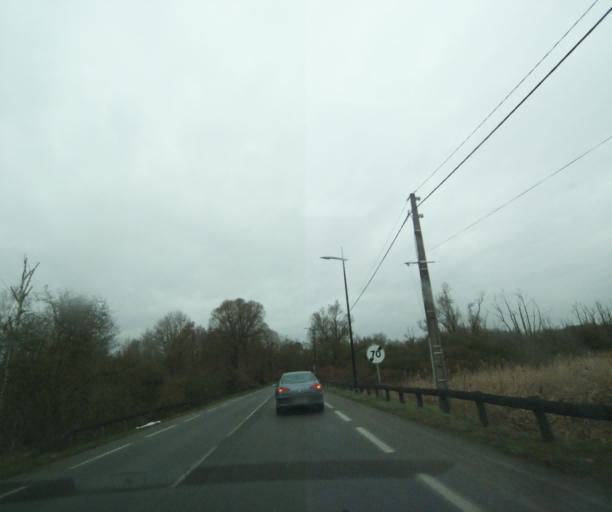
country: FR
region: Nord-Pas-de-Calais
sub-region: Departement du Nord
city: Fresnes-sur-Escaut
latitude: 50.4227
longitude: 3.5833
